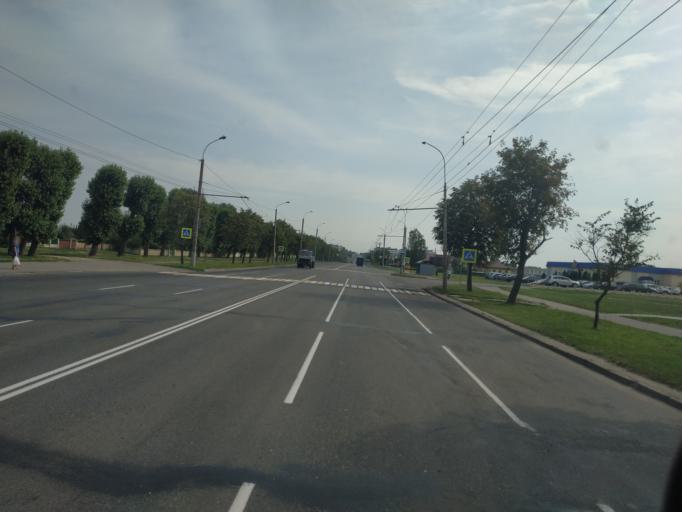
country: BY
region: Mogilev
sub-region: Mahilyowski Rayon
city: Veyno
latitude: 53.8662
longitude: 30.3616
